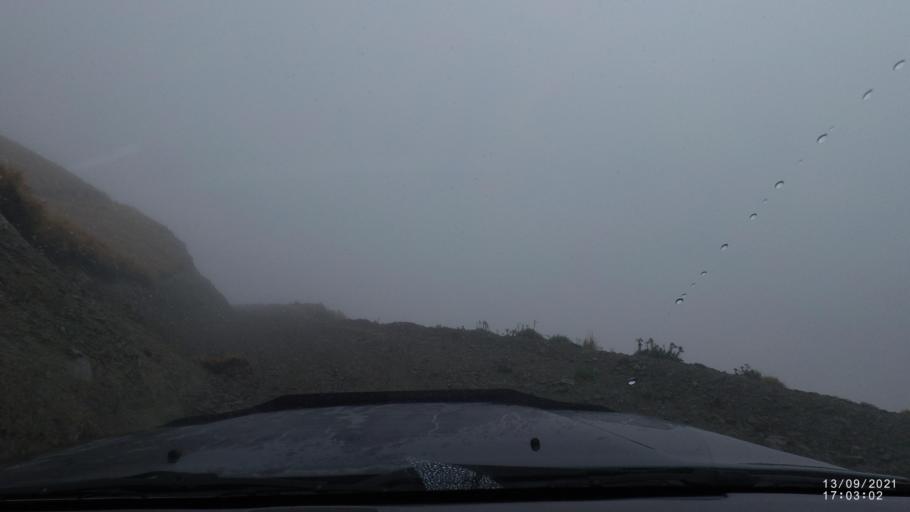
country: BO
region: Cochabamba
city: Colomi
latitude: -17.3201
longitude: -65.7231
